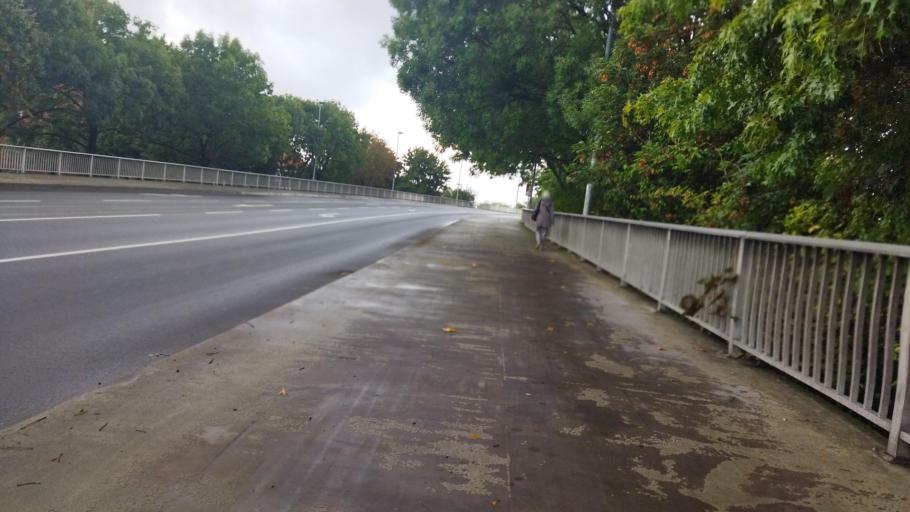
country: DE
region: Lower Saxony
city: Emden
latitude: 53.3689
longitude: 7.1938
